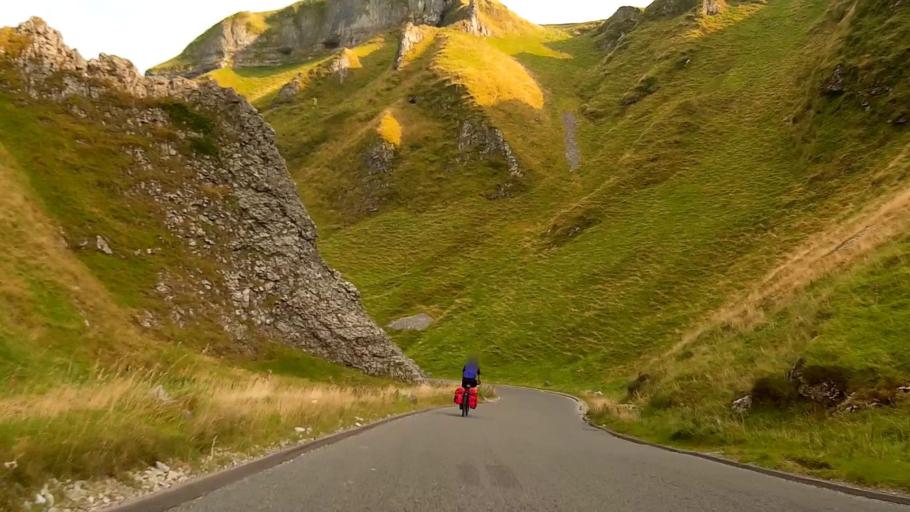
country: GB
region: England
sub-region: Derbyshire
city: Hope Valley
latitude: 53.3404
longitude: -1.7981
